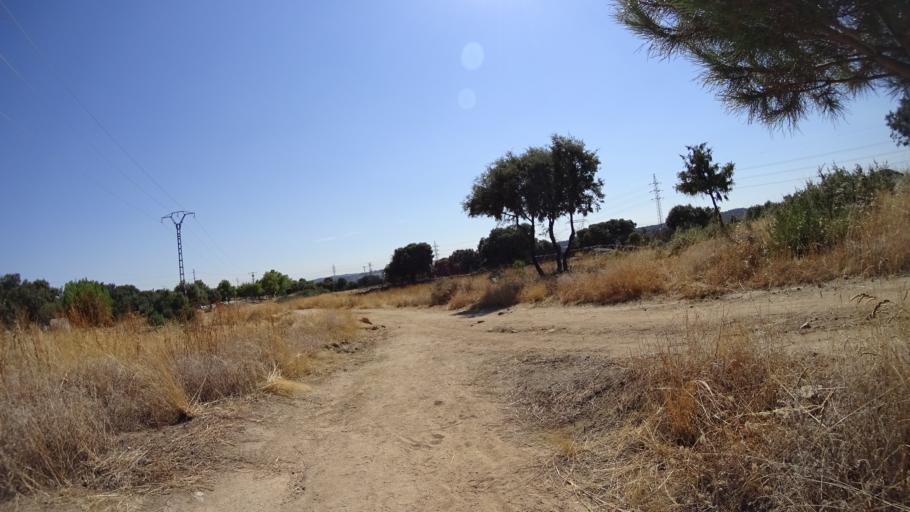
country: ES
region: Madrid
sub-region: Provincia de Madrid
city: Galapagar
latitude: 40.5994
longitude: -4.0122
